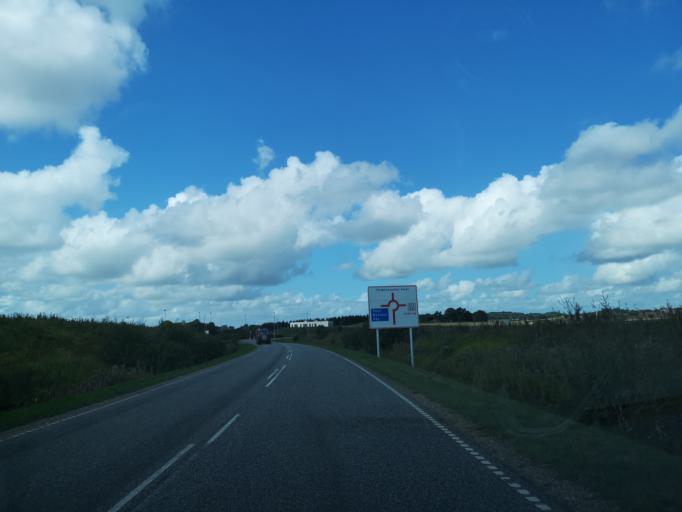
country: DK
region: Central Jutland
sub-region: Holstebro Kommune
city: Holstebro
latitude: 56.3913
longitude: 8.5863
